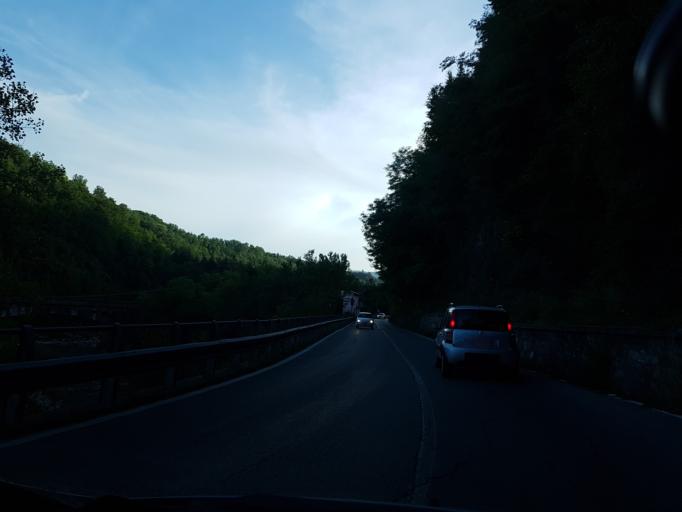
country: IT
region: Tuscany
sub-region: Provincia di Massa-Carrara
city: Pallerone
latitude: 44.2046
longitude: 10.0652
